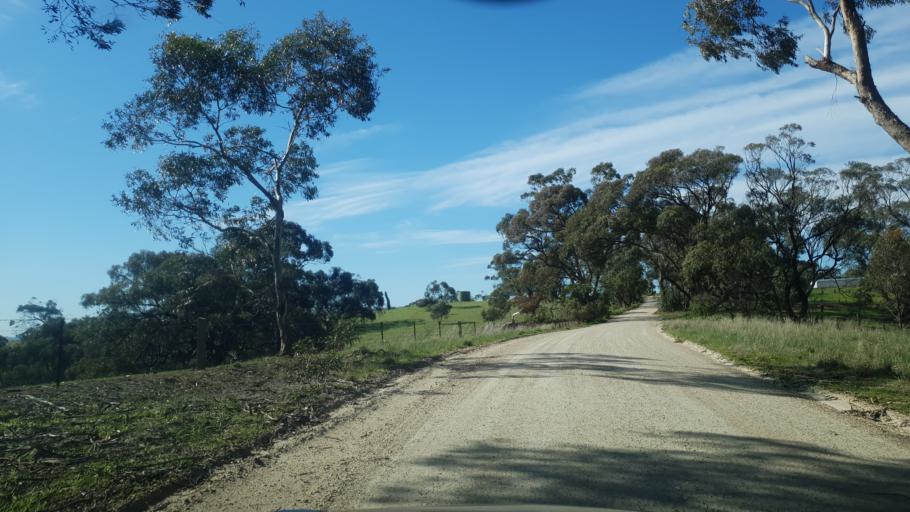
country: AU
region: South Australia
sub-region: Gawler
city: Gawler
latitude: -34.6398
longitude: 138.8107
